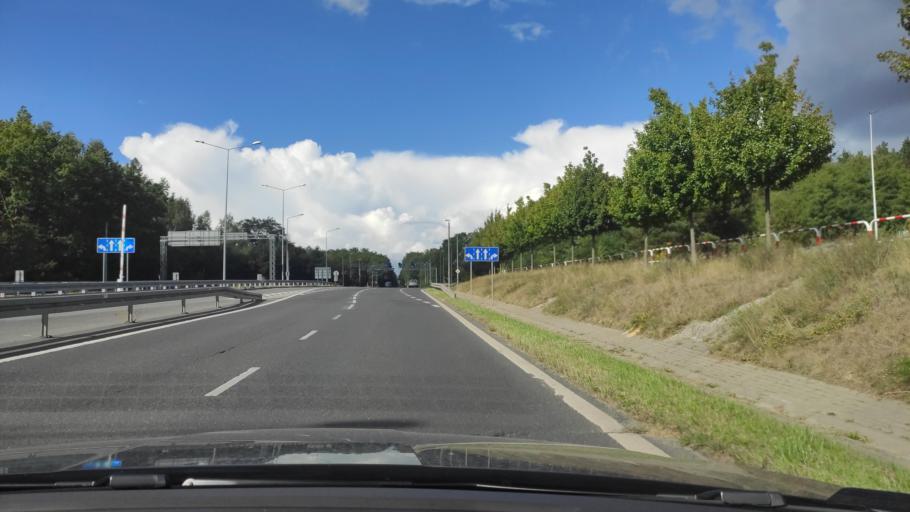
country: PL
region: Greater Poland Voivodeship
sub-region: Powiat poznanski
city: Swarzedz
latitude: 52.4143
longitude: 17.0241
